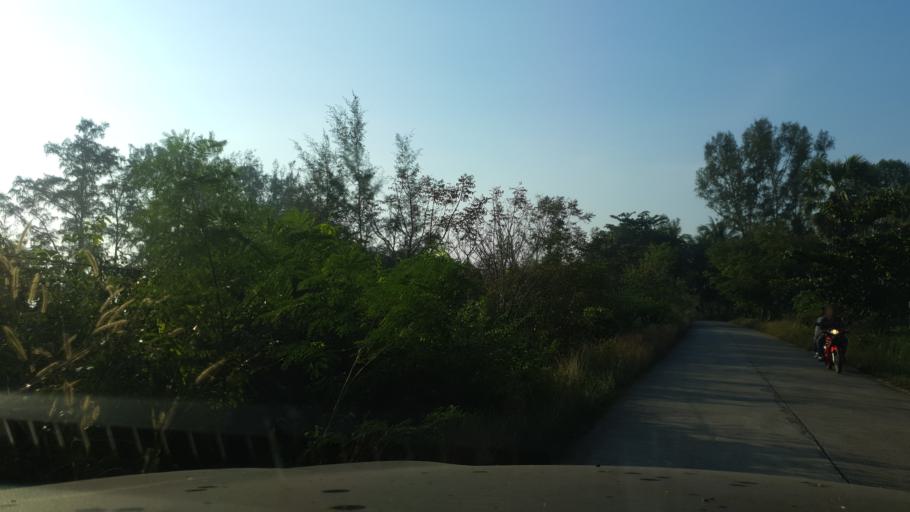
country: TH
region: Prachuap Khiri Khan
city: Bang Saphan
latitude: 11.2866
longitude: 99.5490
